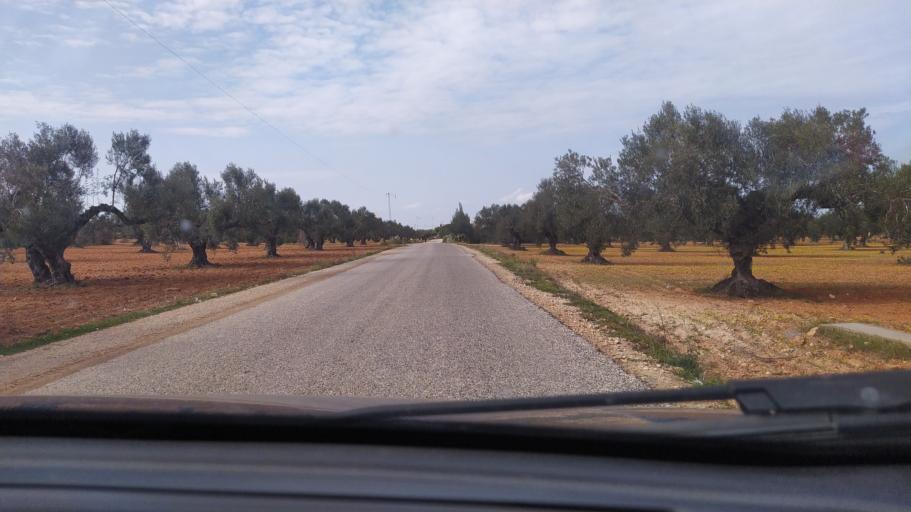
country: TN
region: Al Munastir
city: Sidi Bin Nur
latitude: 35.5287
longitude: 10.9638
